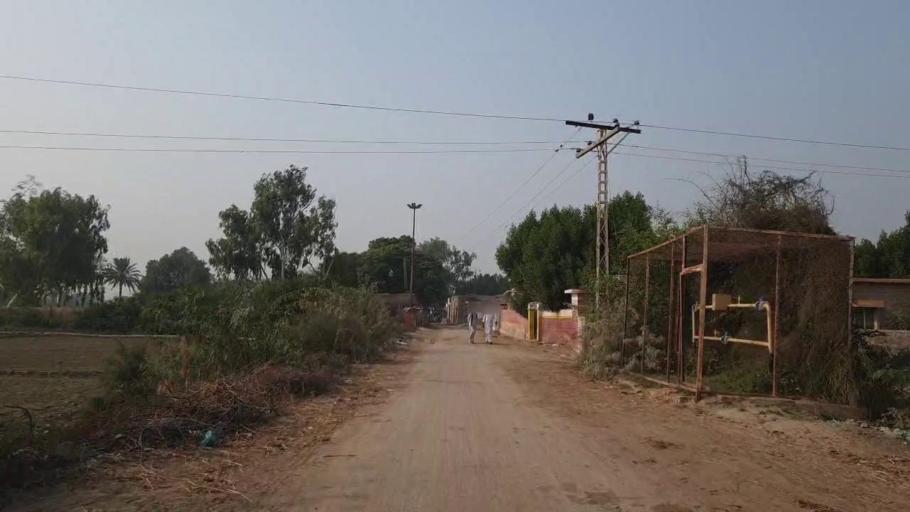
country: PK
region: Sindh
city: Tando Muhammad Khan
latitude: 25.1413
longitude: 68.6121
